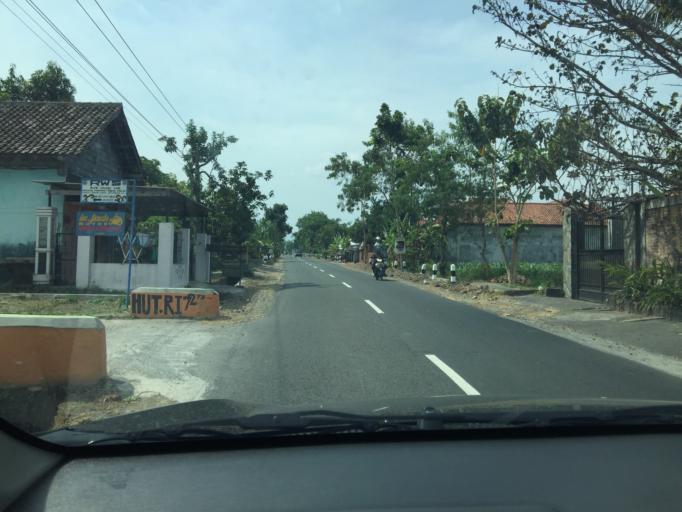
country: ID
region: Central Java
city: Candi Prambanan
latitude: -7.7493
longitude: 110.4812
